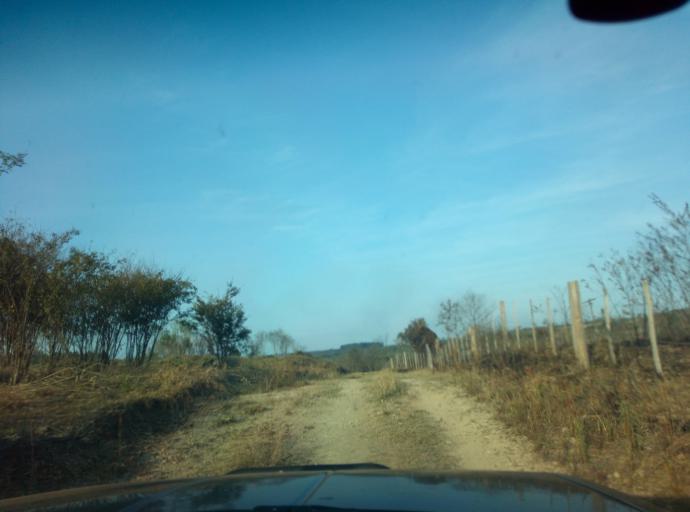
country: PY
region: Caaguazu
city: Yhu
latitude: -25.1995
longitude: -56.1161
